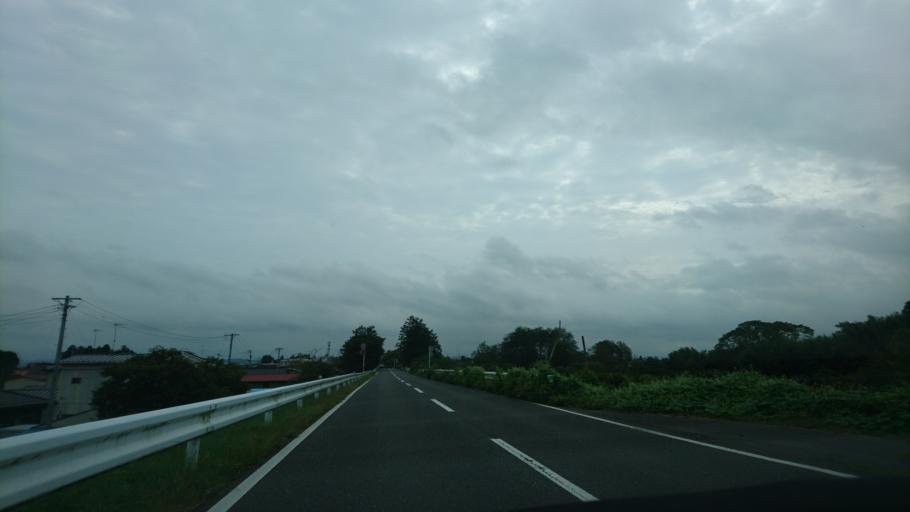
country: JP
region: Iwate
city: Ichinoseki
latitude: 38.7768
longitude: 141.1215
